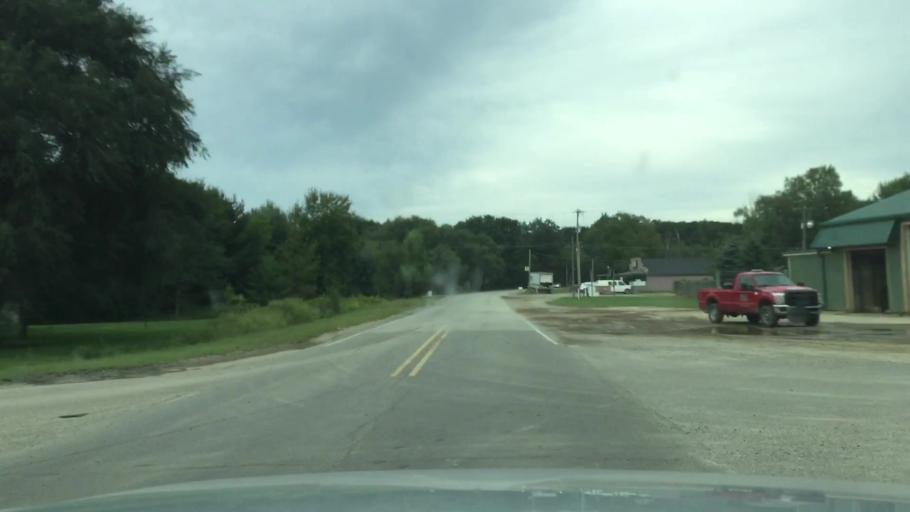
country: US
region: Michigan
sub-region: Genesee County
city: Argentine
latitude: 42.8118
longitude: -83.8951
